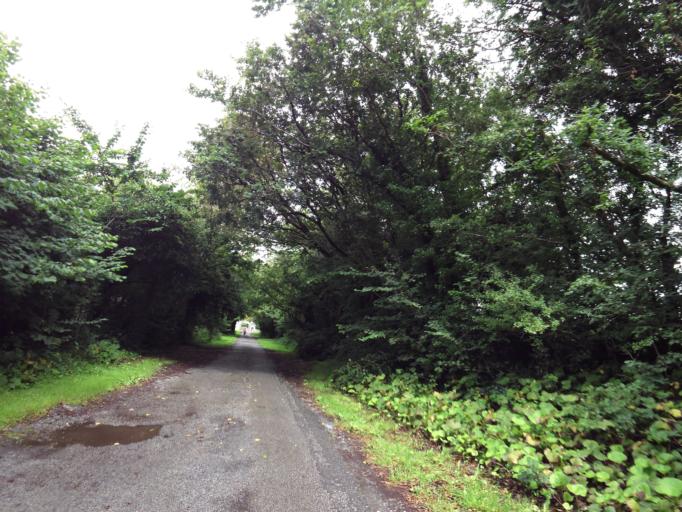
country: IE
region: Connaught
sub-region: County Galway
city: Gaillimh
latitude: 53.2990
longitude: -9.0727
